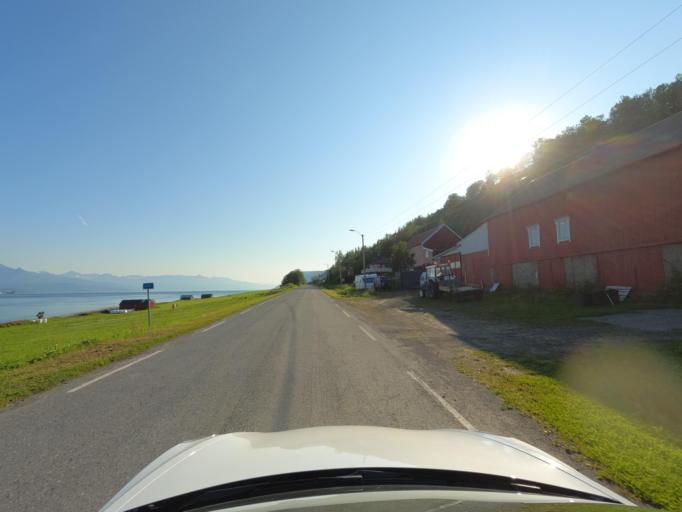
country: NO
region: Nordland
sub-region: Narvik
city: Narvik
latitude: 68.5287
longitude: 17.4616
